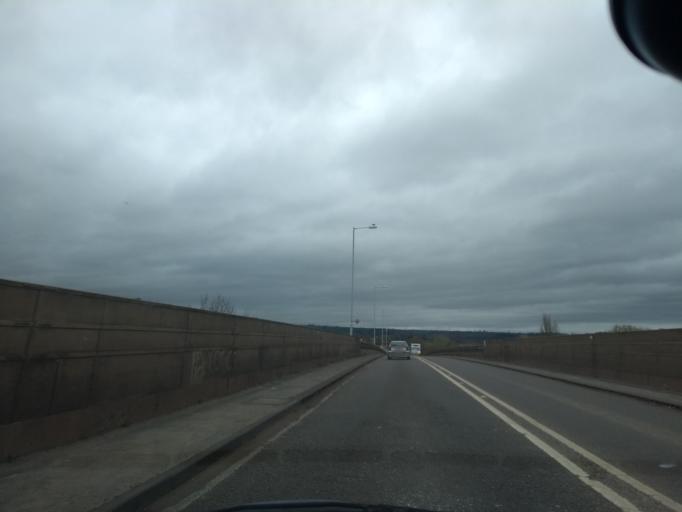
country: GB
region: England
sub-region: Somerset
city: Taunton
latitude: 51.0239
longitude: -3.0901
